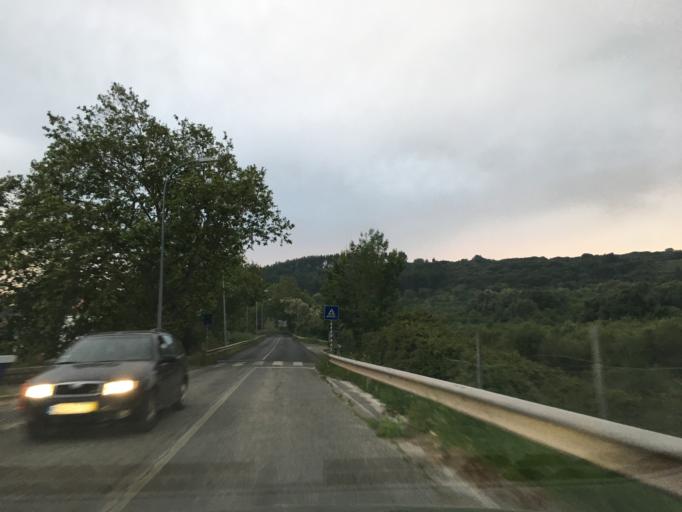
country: PT
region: Lisbon
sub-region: Oeiras
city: Carnaxide
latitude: 38.7303
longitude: -9.2440
